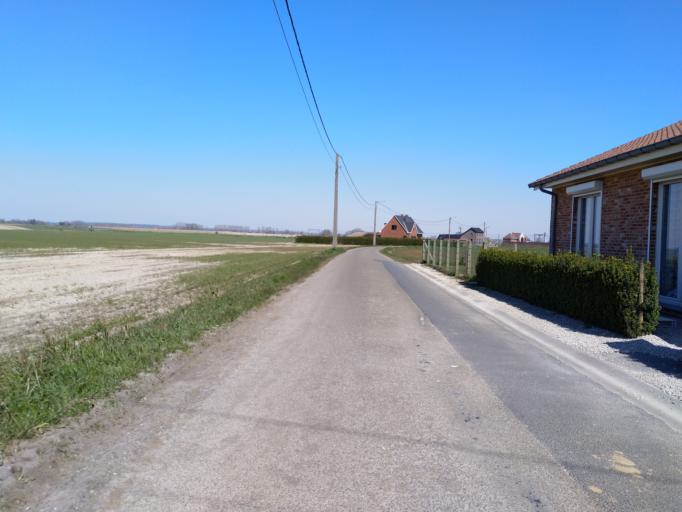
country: BE
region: Wallonia
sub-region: Province du Hainaut
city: Jurbise
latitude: 50.5359
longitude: 3.9115
